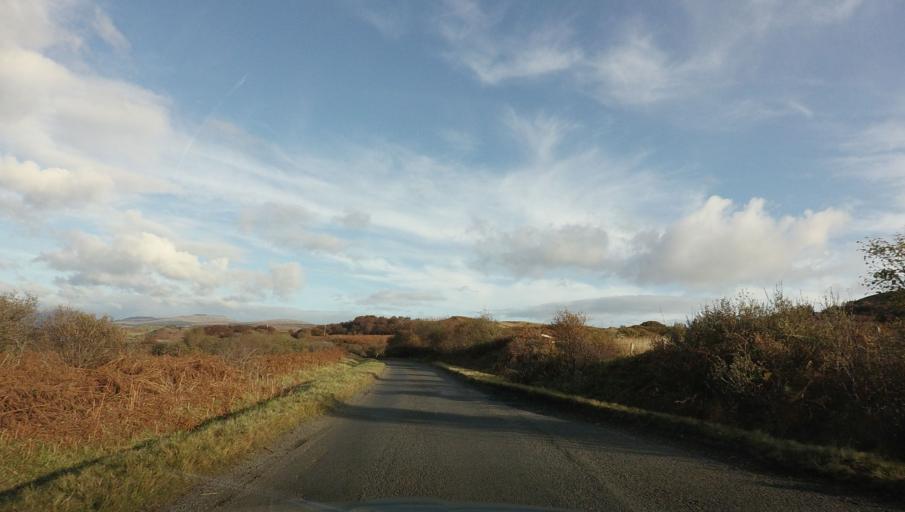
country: GB
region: Scotland
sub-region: Argyll and Bute
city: Isle Of Mull
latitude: 56.3434
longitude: -6.1148
